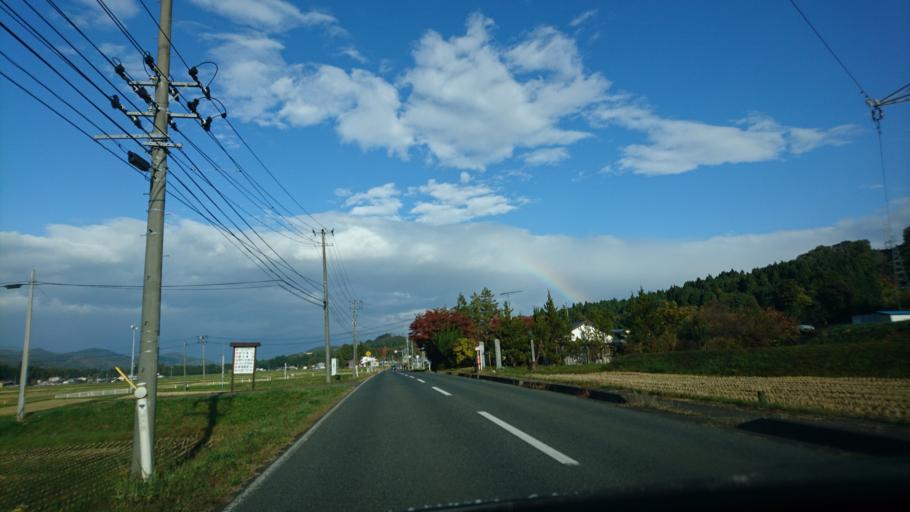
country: JP
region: Iwate
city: Mizusawa
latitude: 39.0278
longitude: 141.0828
